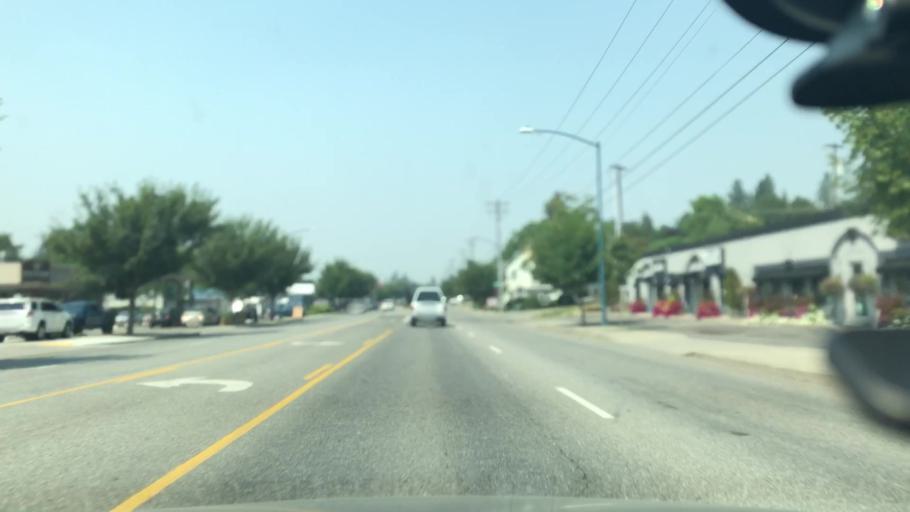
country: US
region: Idaho
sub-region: Kootenai County
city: Coeur d'Alene
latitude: 47.6893
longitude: -116.7988
